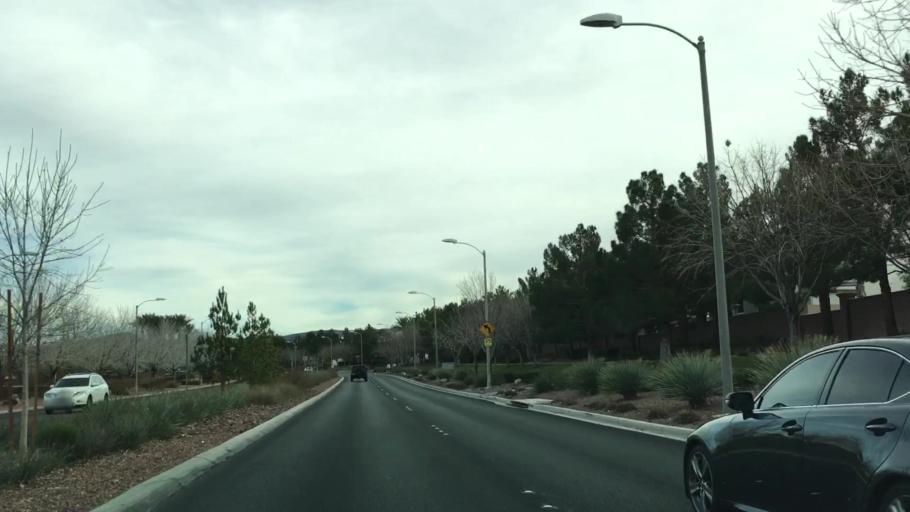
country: US
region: Nevada
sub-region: Clark County
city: Whitney
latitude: 36.0194
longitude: -115.0962
